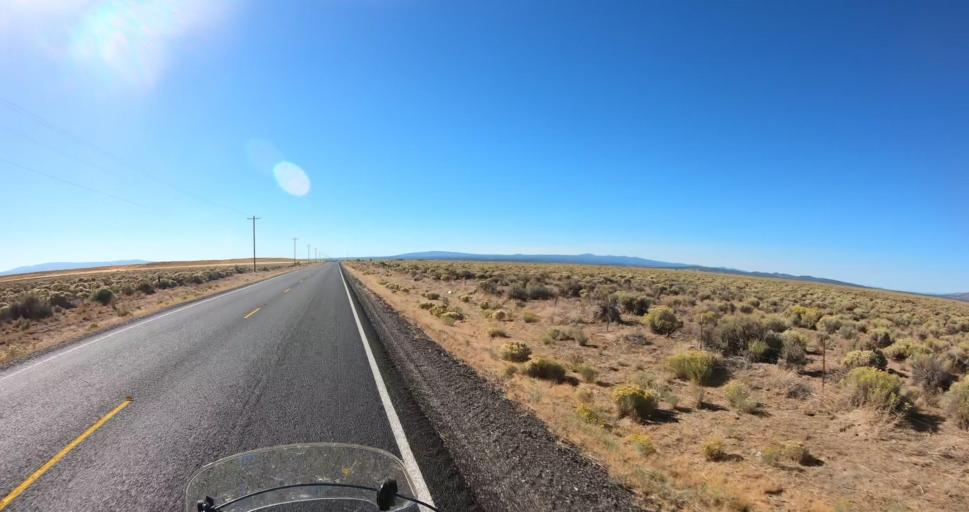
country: US
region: Oregon
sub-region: Deschutes County
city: La Pine
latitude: 43.1290
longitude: -120.9568
